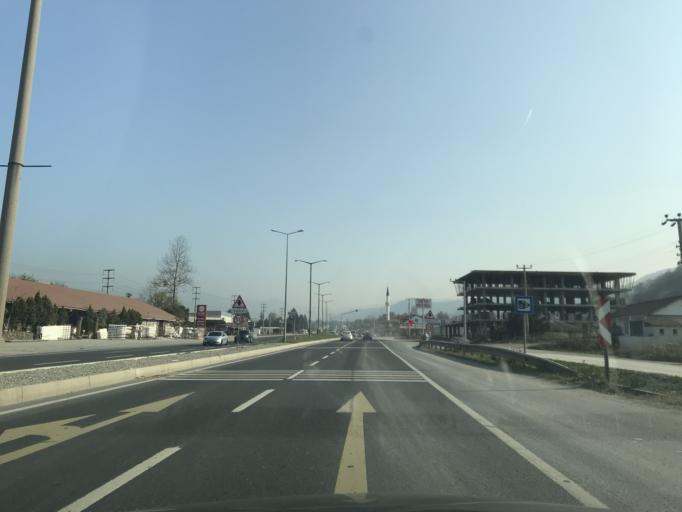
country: TR
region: Duzce
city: Kaynasli
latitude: 40.7790
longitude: 31.2864
